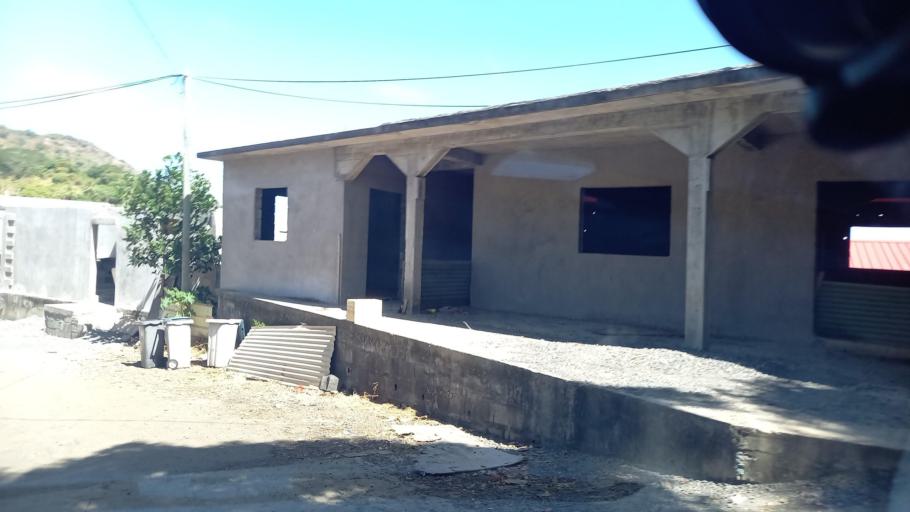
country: YT
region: Kani-Keli
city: Kani Keli
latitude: -12.9644
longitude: 45.1127
